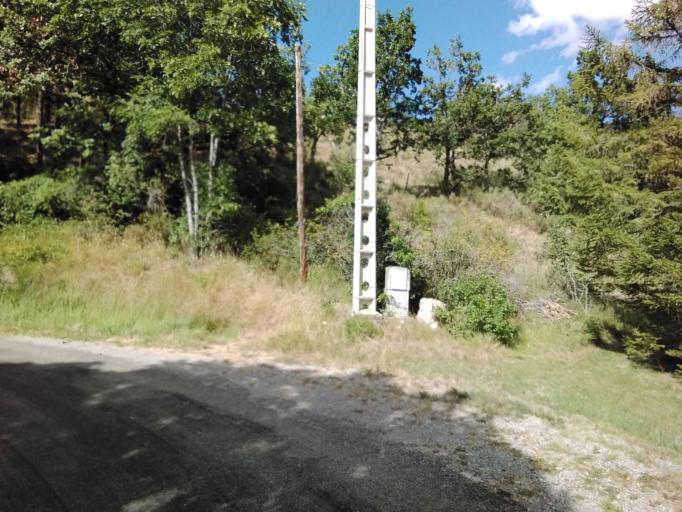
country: FR
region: Provence-Alpes-Cote d'Azur
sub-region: Departement des Hautes-Alpes
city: La Batie-Neuve
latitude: 44.5881
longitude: 6.1513
